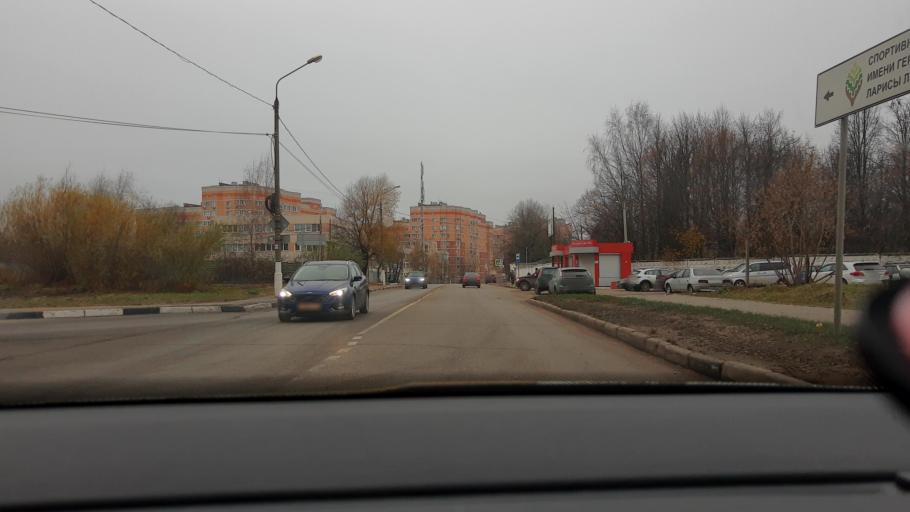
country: RU
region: Moskovskaya
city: Odintsovo
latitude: 55.6867
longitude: 37.2593
